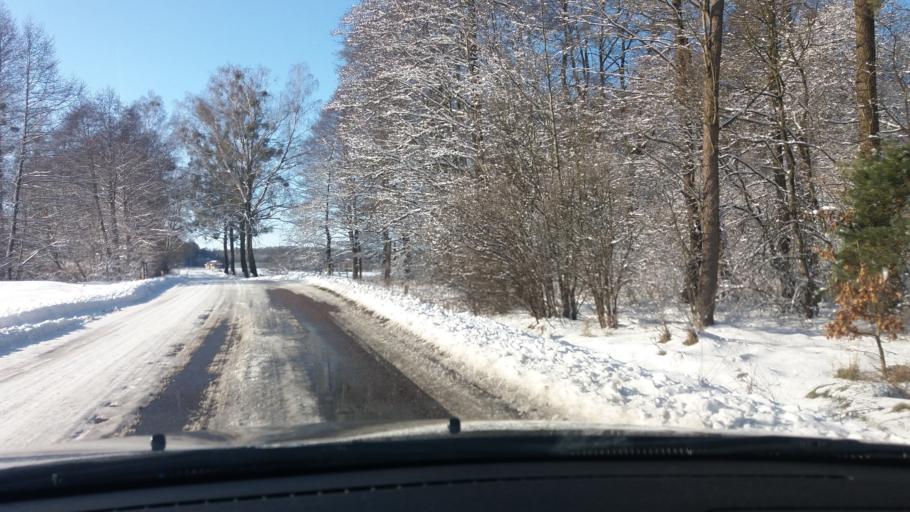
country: PL
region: Masovian Voivodeship
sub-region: Powiat mlawski
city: Dzierzgowo
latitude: 53.3339
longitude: 20.6286
